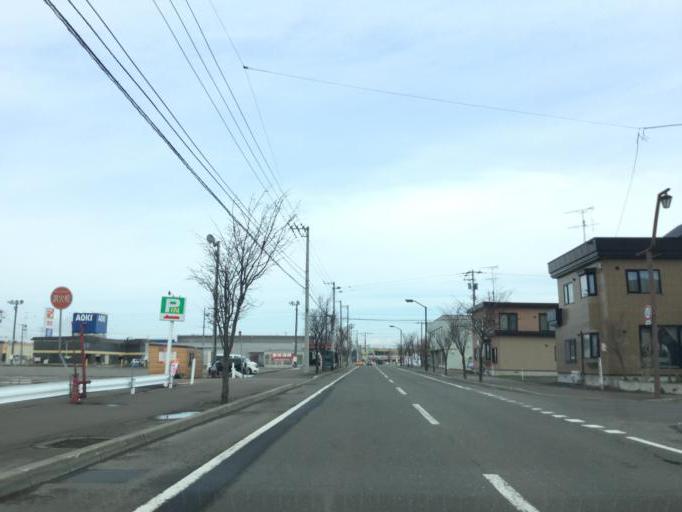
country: JP
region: Hokkaido
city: Iwamizawa
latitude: 43.1876
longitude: 141.7403
